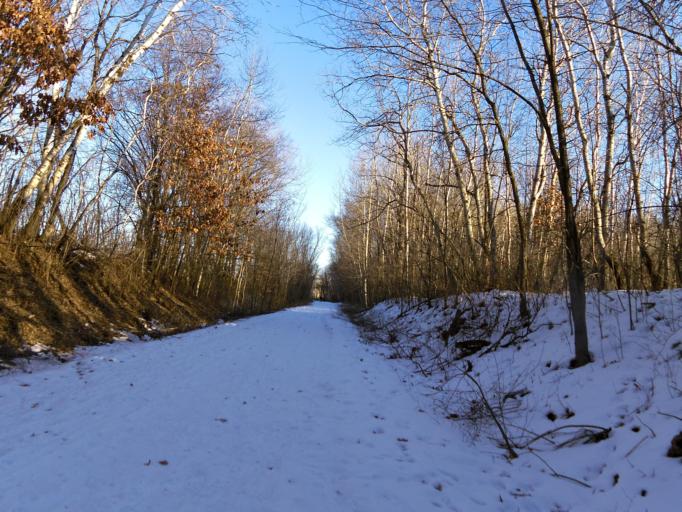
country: US
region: Minnesota
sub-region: Washington County
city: Stillwater
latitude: 45.0710
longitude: -92.8504
